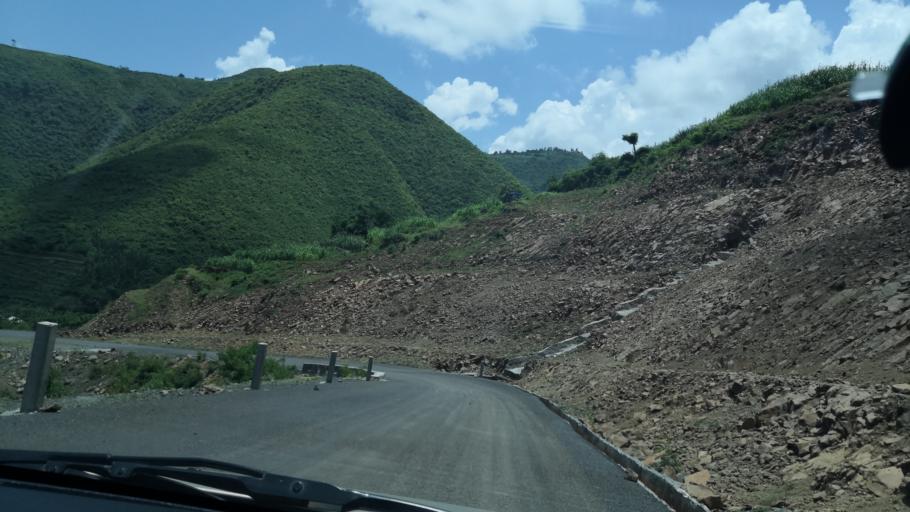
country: ET
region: Amhara
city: Abomsa
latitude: 10.3036
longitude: 39.8892
